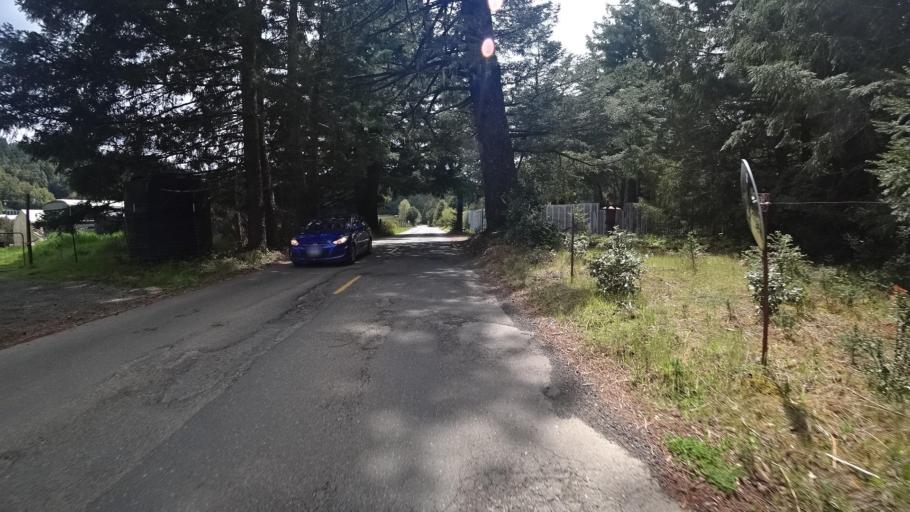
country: US
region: California
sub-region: Humboldt County
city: Redway
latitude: 40.0387
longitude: -123.9575
